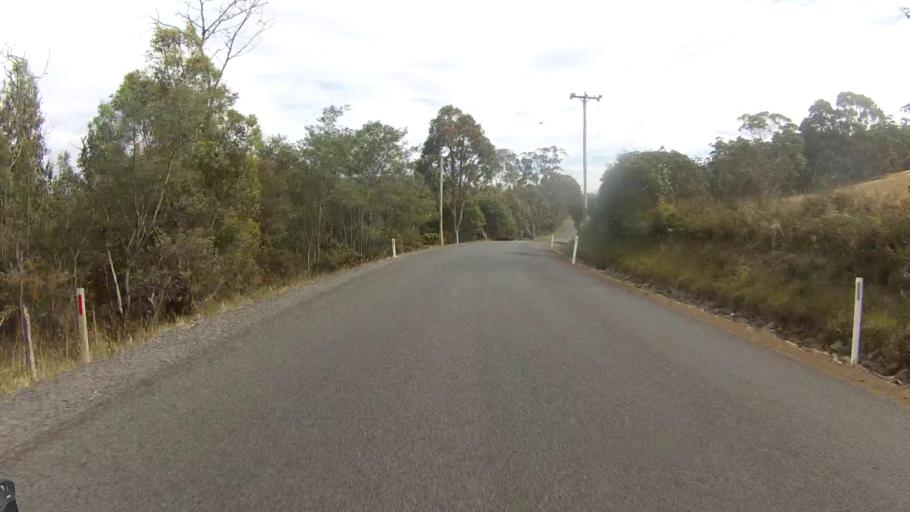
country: AU
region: Tasmania
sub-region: Sorell
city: Sorell
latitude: -42.8047
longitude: 147.7933
